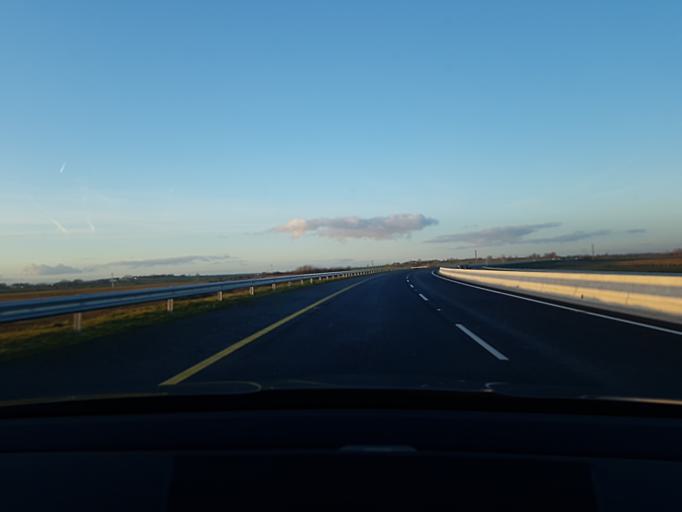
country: IE
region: Connaught
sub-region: County Galway
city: Tuam
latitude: 53.4695
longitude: -8.8629
